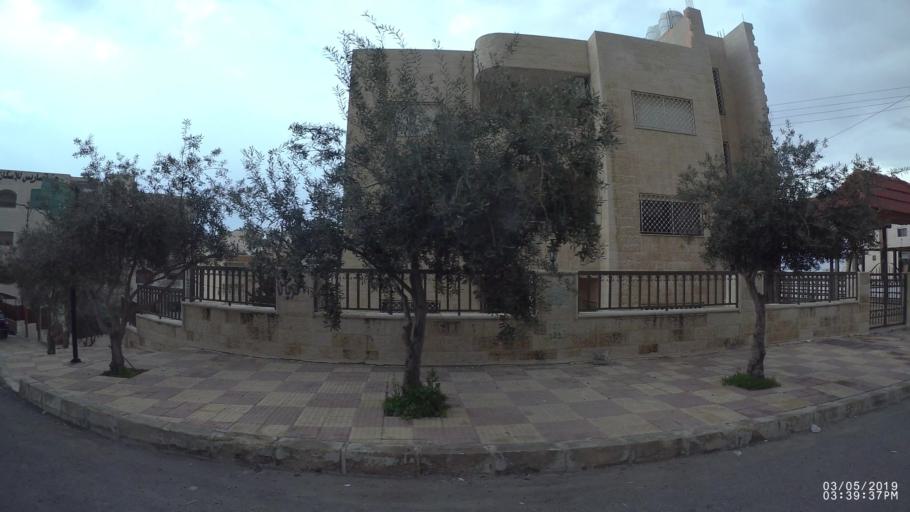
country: JO
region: Amman
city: Amman
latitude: 32.0069
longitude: 35.9430
